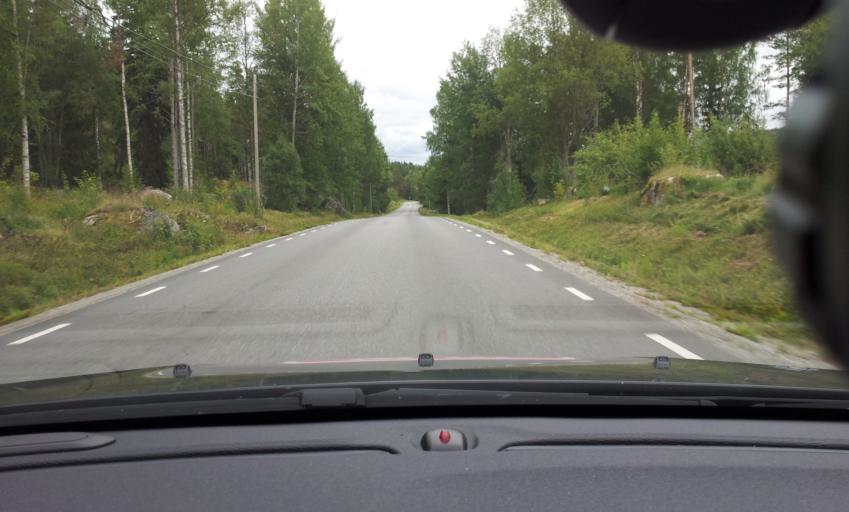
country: SE
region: Jaemtland
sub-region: Braecke Kommun
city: Braecke
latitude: 62.9669
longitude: 15.1717
